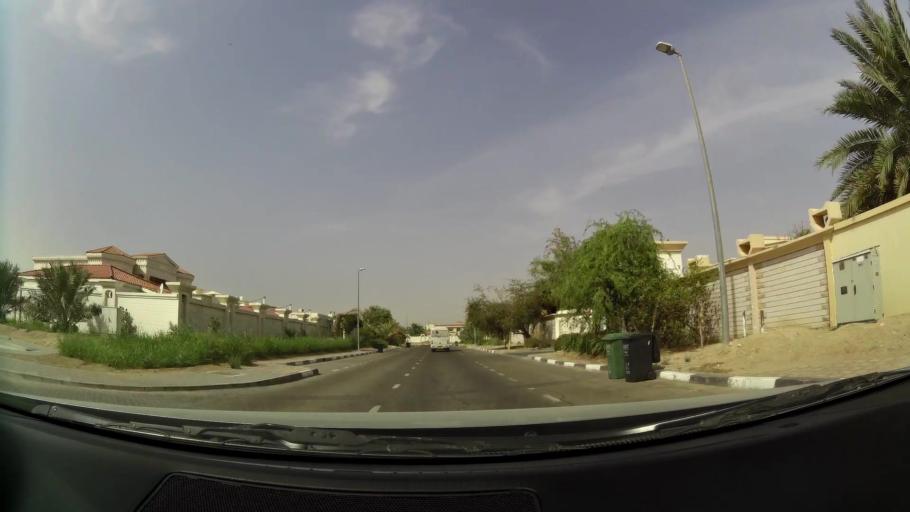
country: AE
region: Abu Dhabi
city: Al Ain
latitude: 24.1480
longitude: 55.7005
